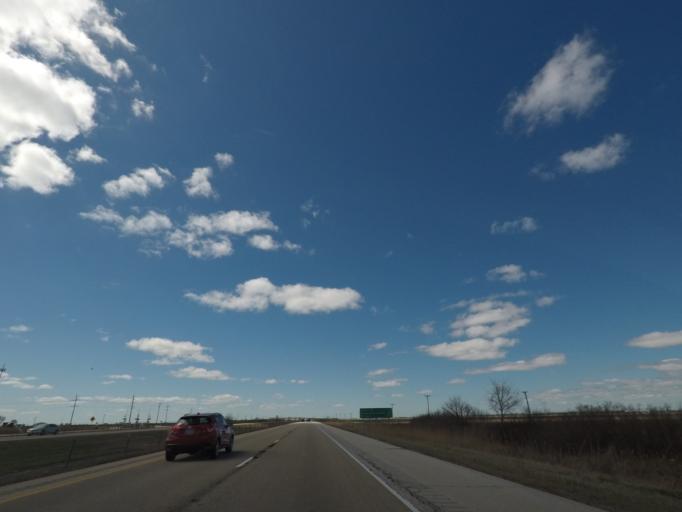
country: US
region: Illinois
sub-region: Grundy County
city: Gardner
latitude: 41.1654
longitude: -88.3378
